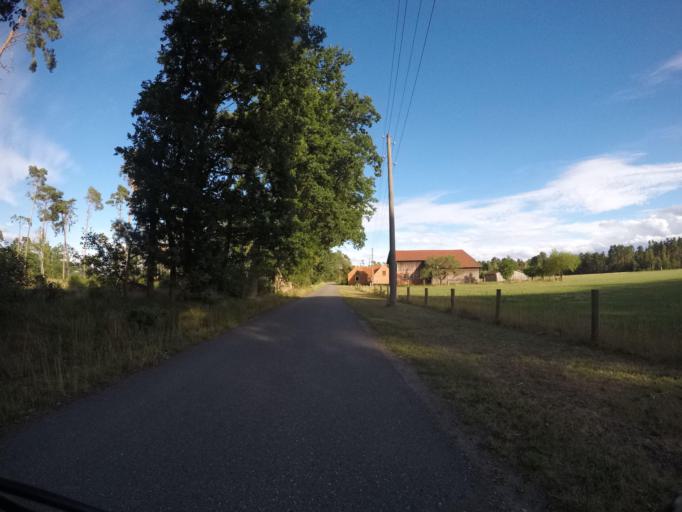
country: DE
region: Mecklenburg-Vorpommern
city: Lubtheen
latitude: 53.2343
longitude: 11.0425
